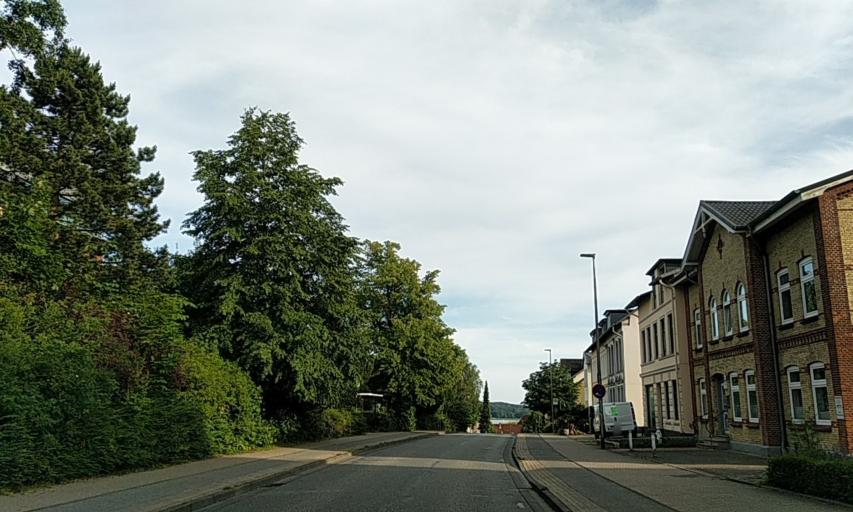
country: DE
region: Schleswig-Holstein
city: Schleswig
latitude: 54.5184
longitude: 9.5583
